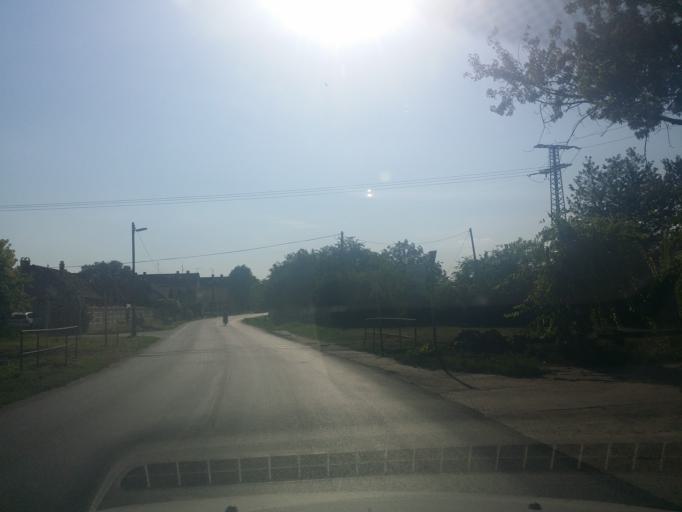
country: HU
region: Bacs-Kiskun
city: Baja
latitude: 46.1713
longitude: 18.9704
